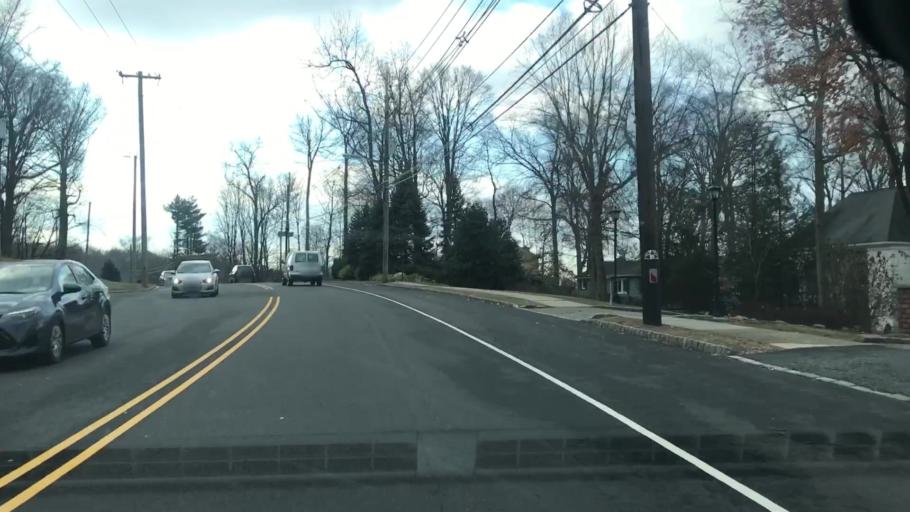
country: US
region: New Jersey
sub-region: Essex County
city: Livingston
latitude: 40.7905
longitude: -74.2990
